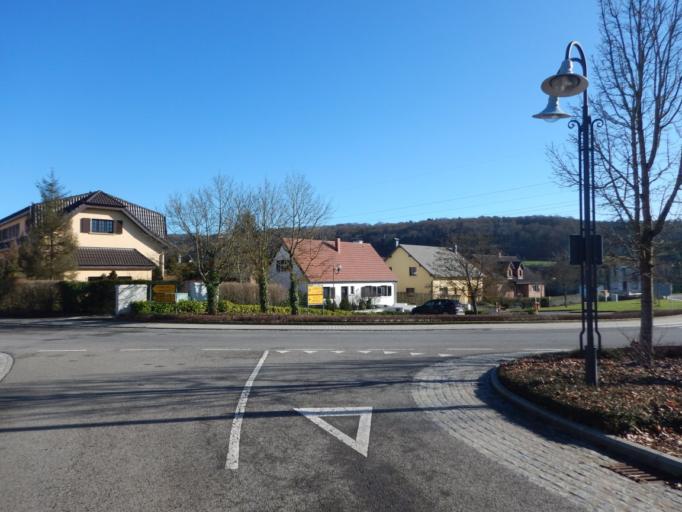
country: LU
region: Luxembourg
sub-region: Canton de Mersch
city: Fischbach
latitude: 49.7006
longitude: 6.1918
